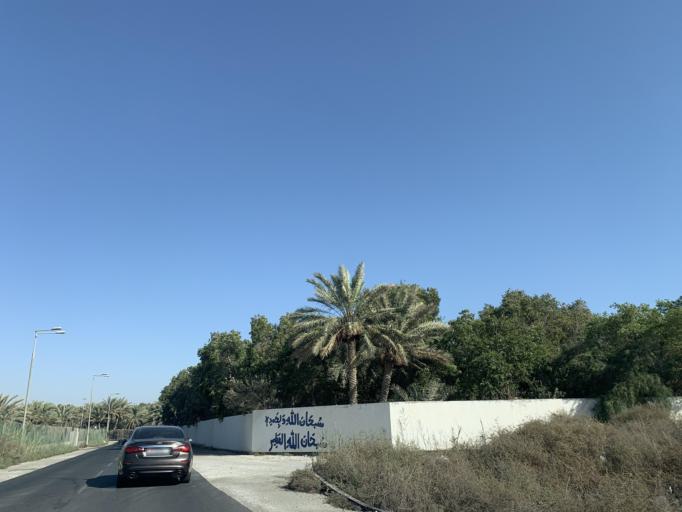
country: BH
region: Manama
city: Jidd Hafs
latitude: 26.2036
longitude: 50.4538
